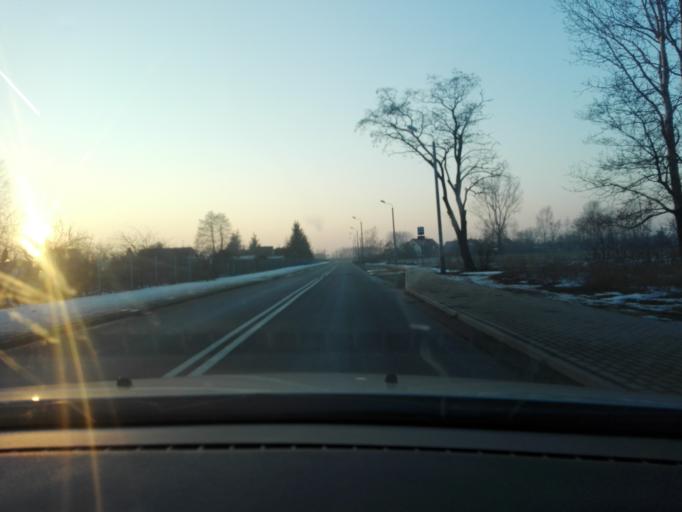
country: PL
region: Lodz Voivodeship
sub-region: Powiat kutnowski
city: Kutno
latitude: 52.2062
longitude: 19.3953
